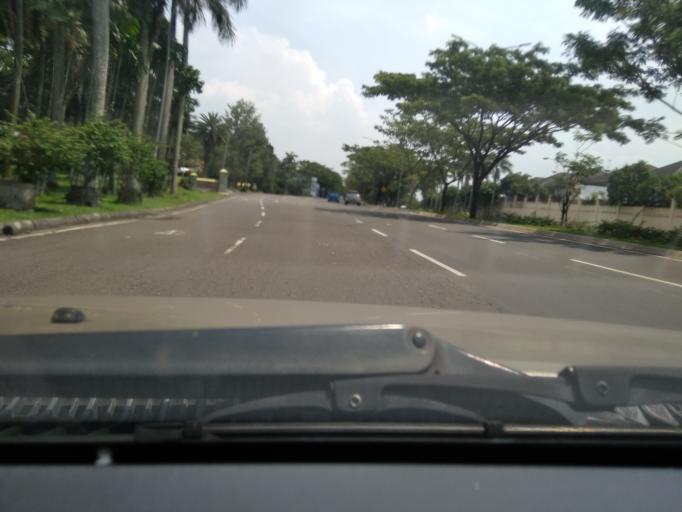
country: ID
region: West Java
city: Serpong
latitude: -6.2801
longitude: 106.6606
